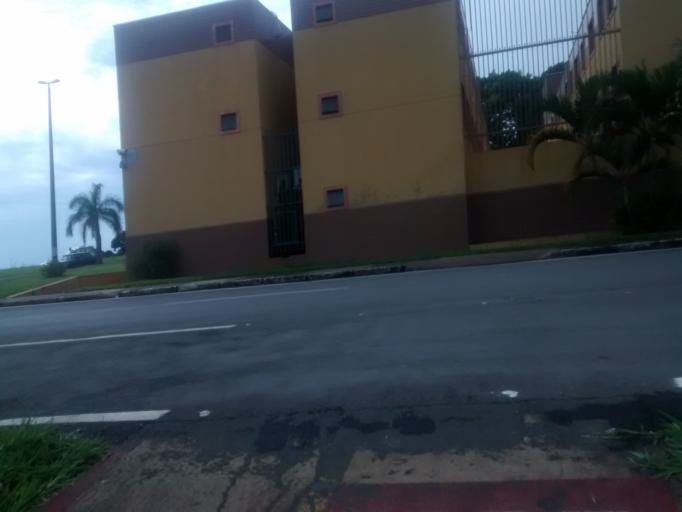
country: BR
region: Federal District
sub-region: Brasilia
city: Brasilia
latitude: -15.7467
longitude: -47.8825
